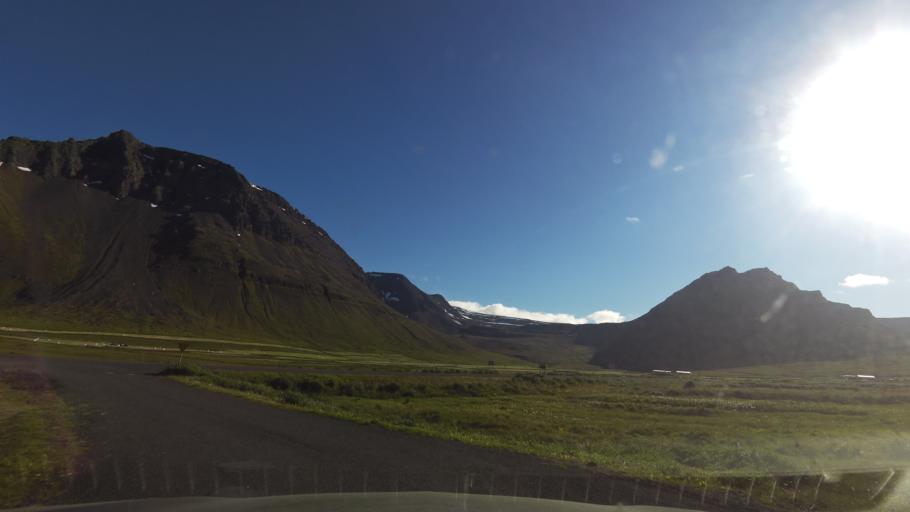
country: IS
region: Westfjords
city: Isafjoerdur
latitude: 66.1593
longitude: -23.2679
